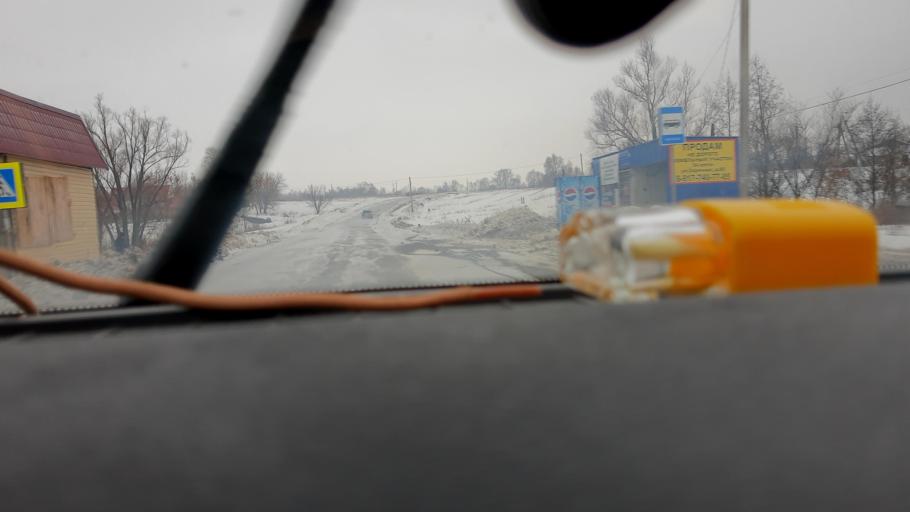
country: RU
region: Bashkortostan
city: Ulukulevo
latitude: 54.5099
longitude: 56.4101
